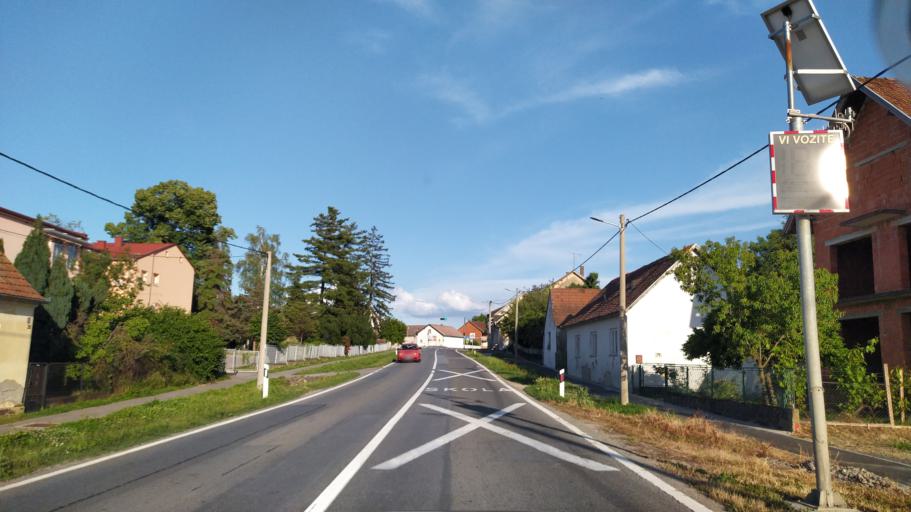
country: HR
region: Virovitick-Podravska
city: Slatina
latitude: 45.6640
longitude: 17.7686
